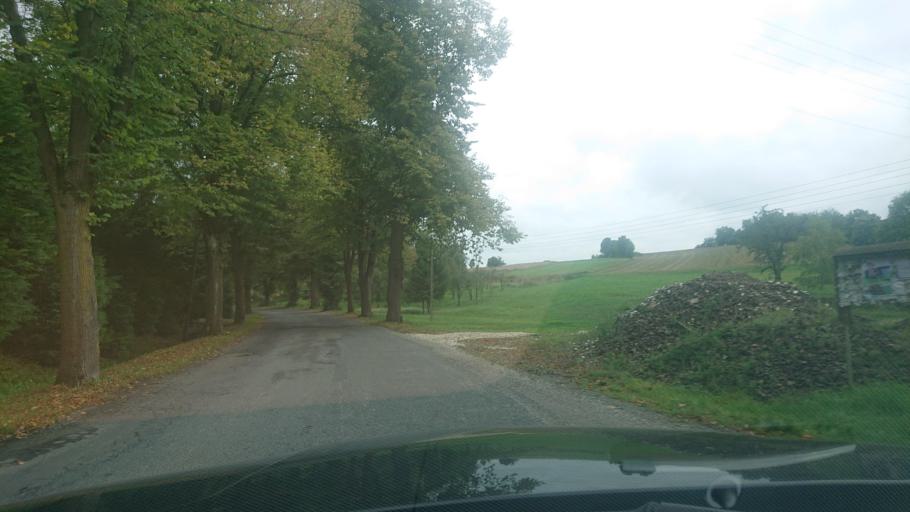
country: PL
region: Lower Silesian Voivodeship
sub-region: Powiat klodzki
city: Bystrzyca Klodzka
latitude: 50.3172
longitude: 16.7298
